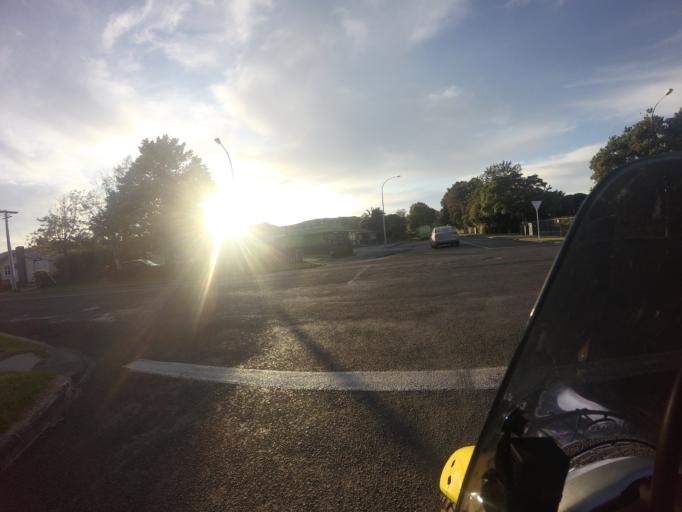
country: NZ
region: Gisborne
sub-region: Gisborne District
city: Gisborne
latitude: -38.6737
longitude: 178.0502
